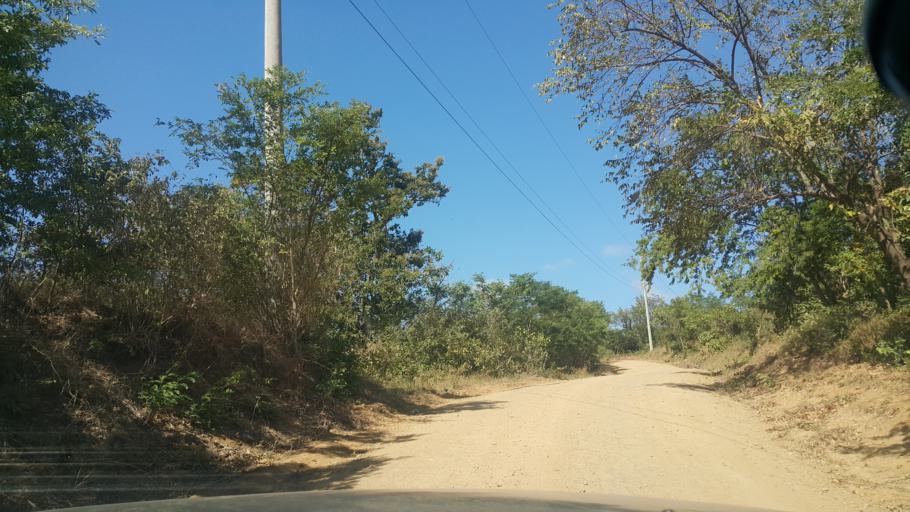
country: NI
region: Rivas
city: San Juan del Sur
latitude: 11.2779
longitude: -85.8874
